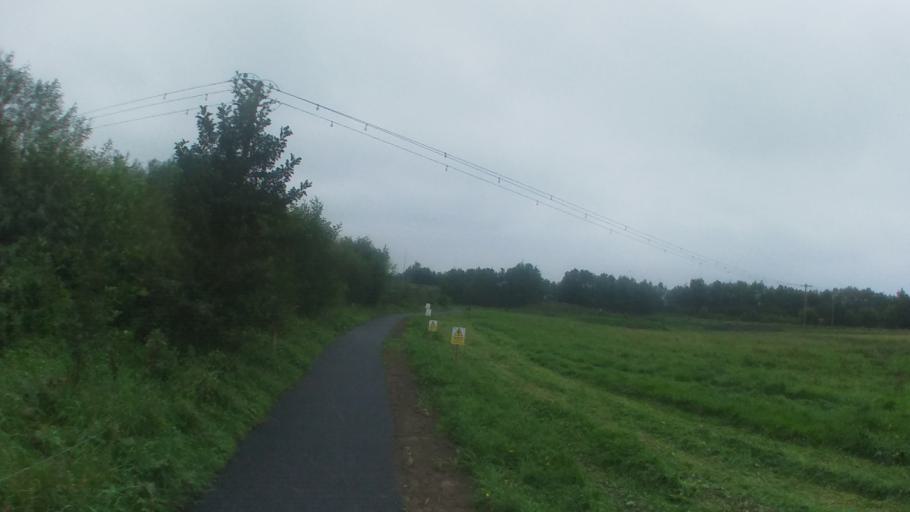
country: IE
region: Leinster
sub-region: Kilkenny
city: Callan
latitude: 52.5466
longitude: -7.3931
